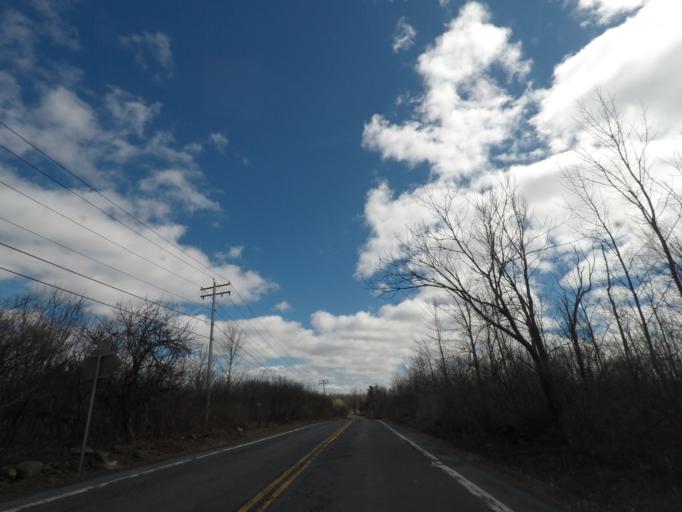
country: US
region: New York
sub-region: Albany County
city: Altamont
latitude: 42.6736
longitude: -74.0722
